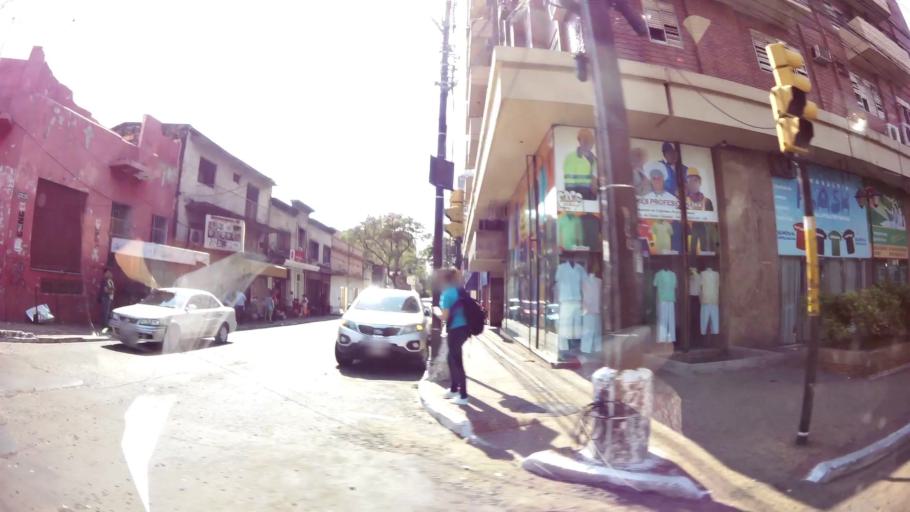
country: PY
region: Asuncion
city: Asuncion
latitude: -25.2883
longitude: -57.6270
